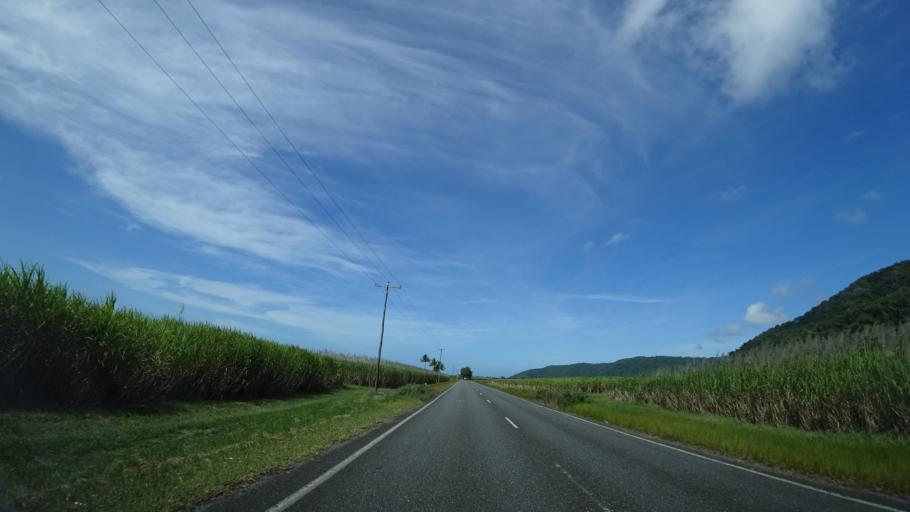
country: AU
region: Queensland
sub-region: Cairns
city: Port Douglas
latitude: -16.2896
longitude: 145.3852
